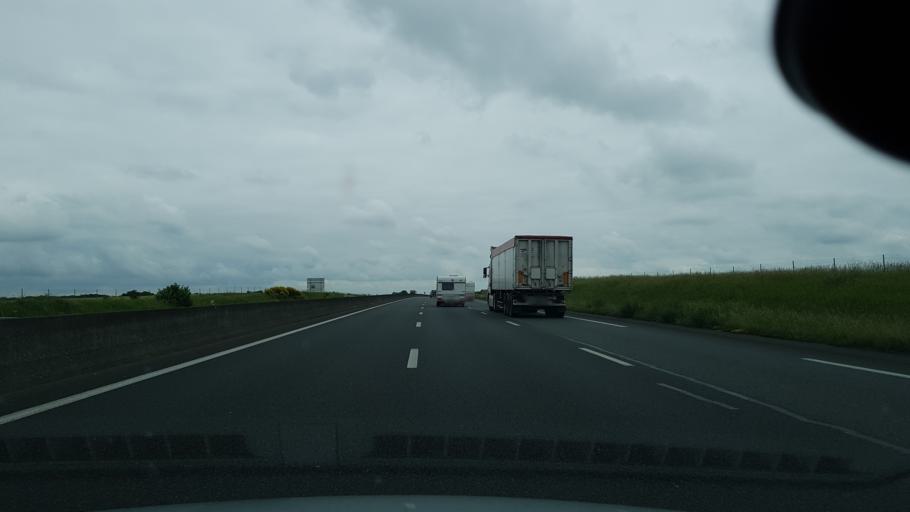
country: FR
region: Centre
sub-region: Departement du Loir-et-Cher
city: La Chaussee-Saint-Victor
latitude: 47.6539
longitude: 1.3771
